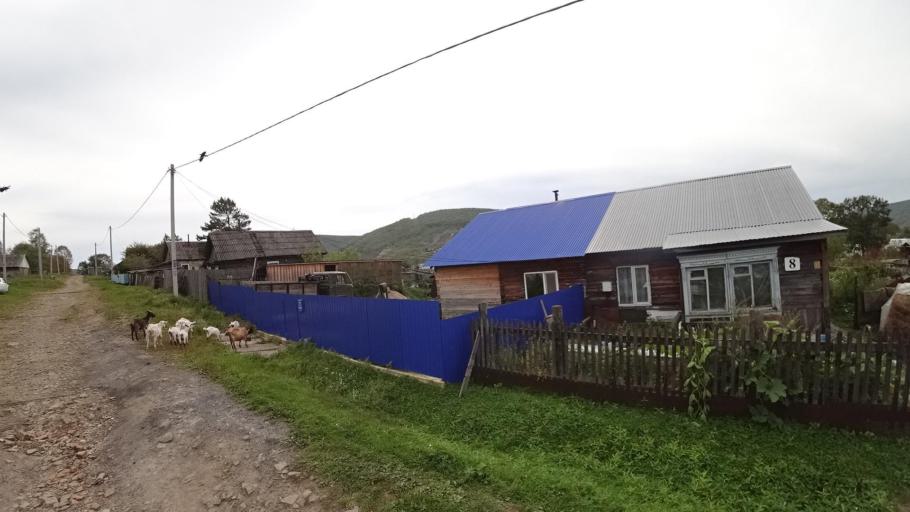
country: RU
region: Jewish Autonomous Oblast
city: Khingansk
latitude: 49.1300
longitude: 131.2012
